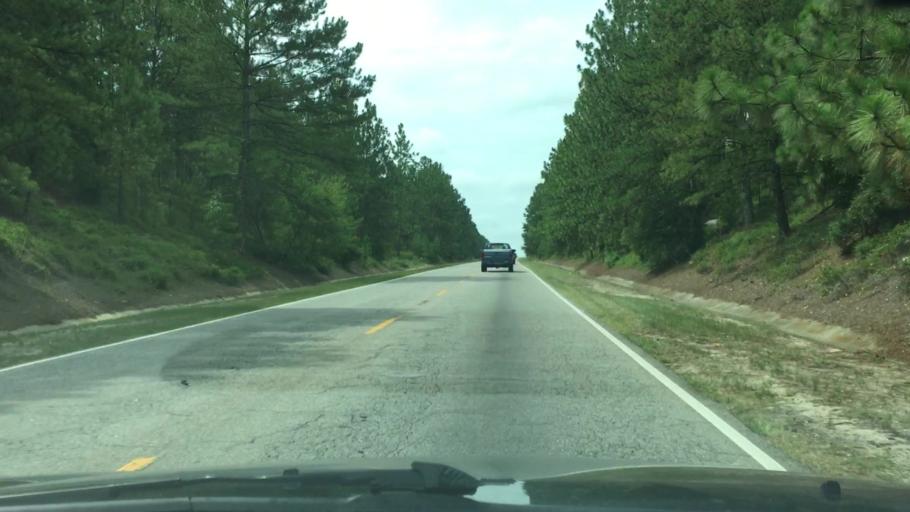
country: US
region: South Carolina
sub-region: Aiken County
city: Warrenville
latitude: 33.5515
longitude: -81.7778
